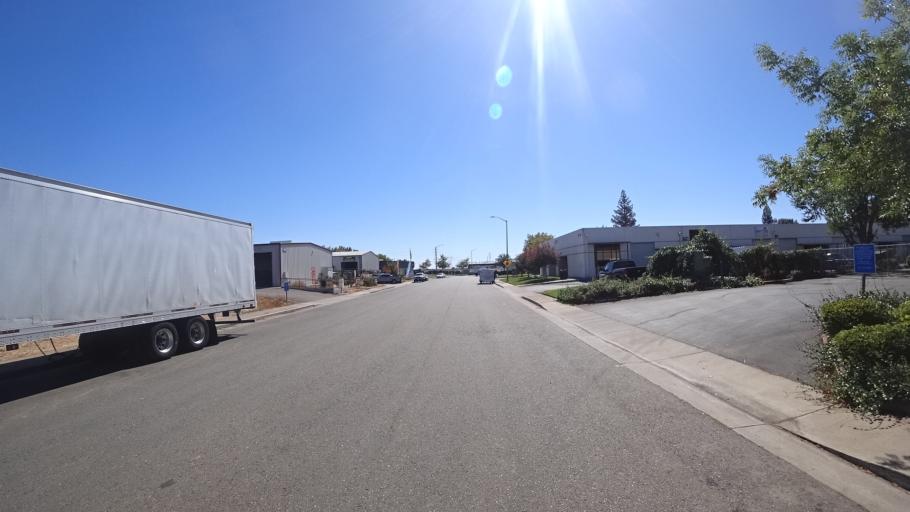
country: US
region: California
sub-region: Sacramento County
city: Elk Grove
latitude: 38.3778
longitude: -121.3577
